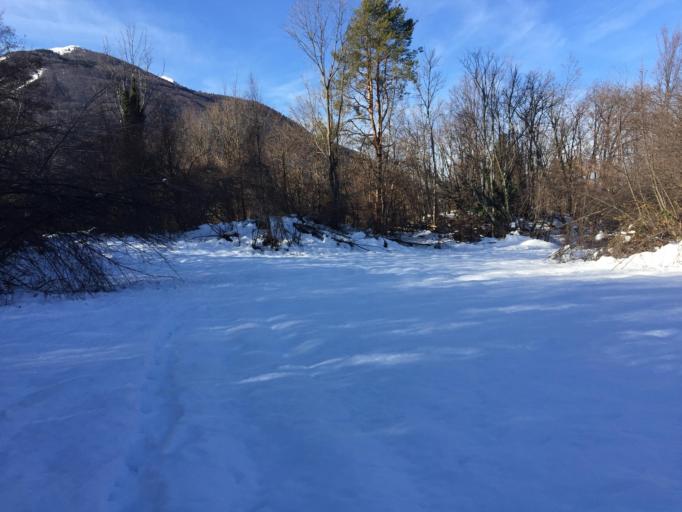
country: IT
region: Friuli Venezia Giulia
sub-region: Provincia di Udine
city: Chiaulis
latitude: 46.3744
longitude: 12.9776
